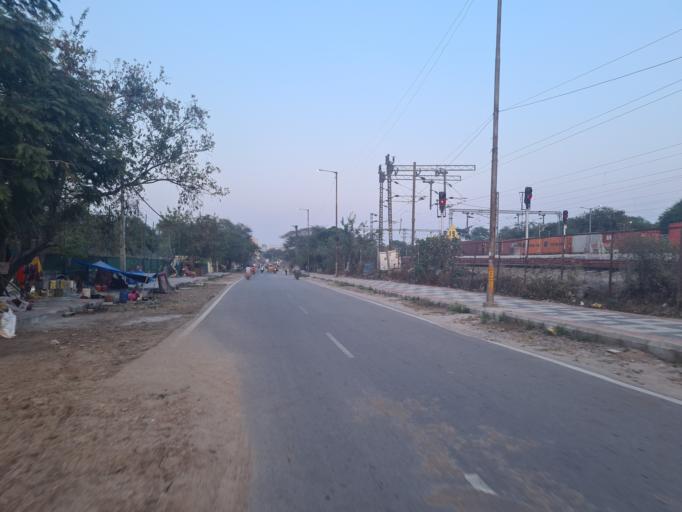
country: IN
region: Telangana
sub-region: Medak
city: Serilingampalle
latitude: 17.4841
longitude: 78.3187
